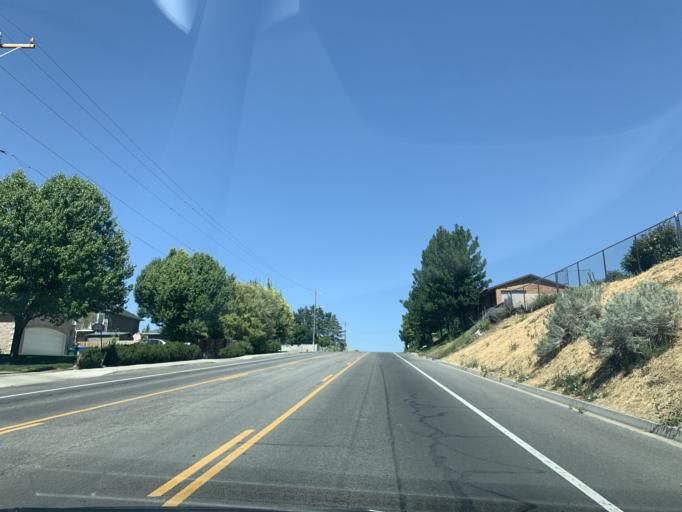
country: US
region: Utah
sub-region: Utah County
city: Lehi
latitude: 40.4046
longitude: -111.8302
